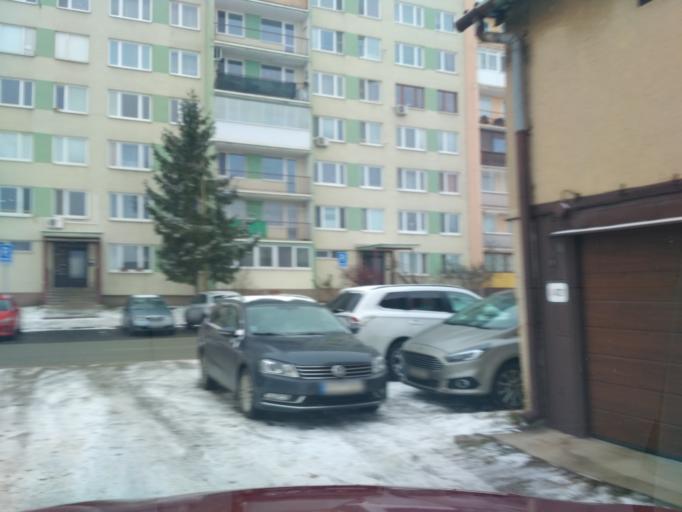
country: SK
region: Kosicky
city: Kosice
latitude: 48.7047
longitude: 21.2343
